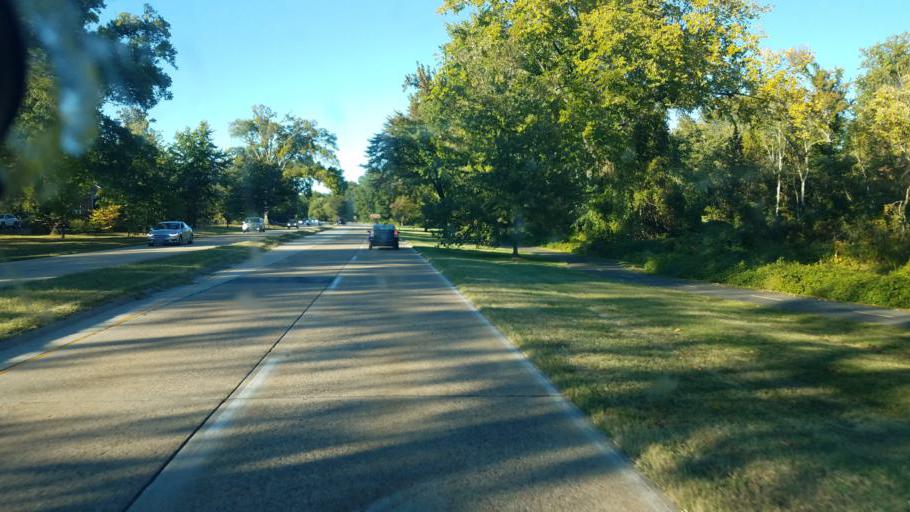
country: US
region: Virginia
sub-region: Fairfax County
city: Belle Haven
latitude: 38.7732
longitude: -77.0521
